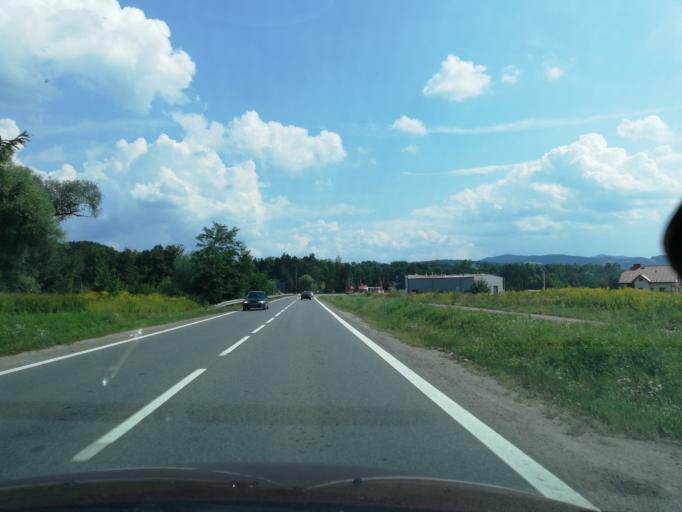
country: PL
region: Lesser Poland Voivodeship
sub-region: Powiat nowosadecki
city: Stary Sacz
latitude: 49.5704
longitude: 20.6532
